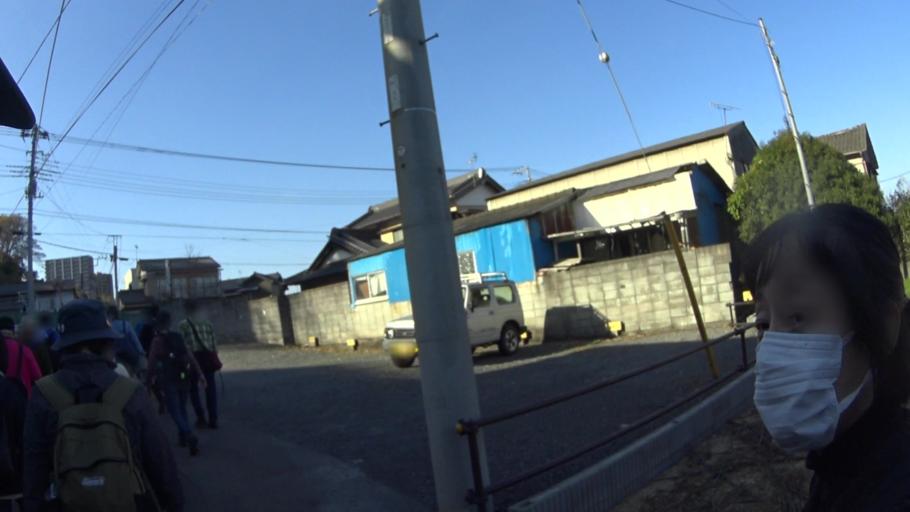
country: JP
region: Ibaraki
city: Mito-shi
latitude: 36.3817
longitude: 140.4718
